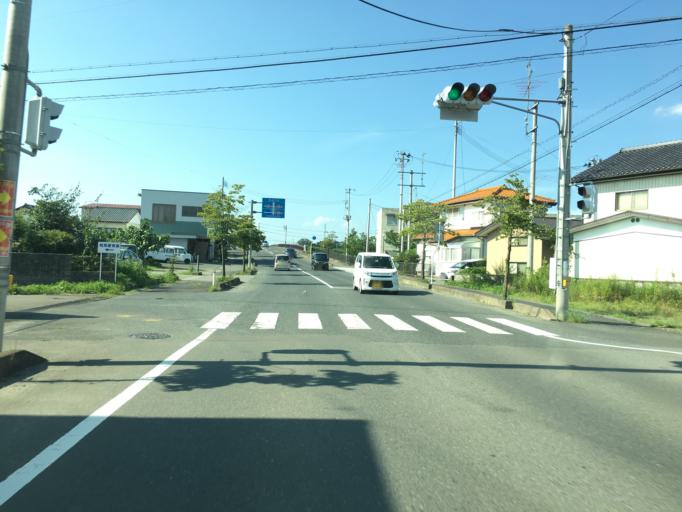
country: JP
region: Miyagi
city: Marumori
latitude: 37.7889
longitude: 140.9132
